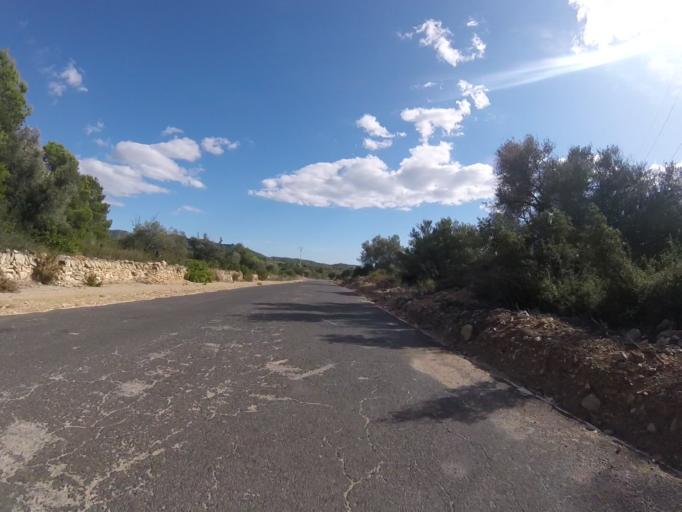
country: ES
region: Valencia
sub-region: Provincia de Castello
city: Alcala de Xivert
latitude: 40.2749
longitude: 0.2308
